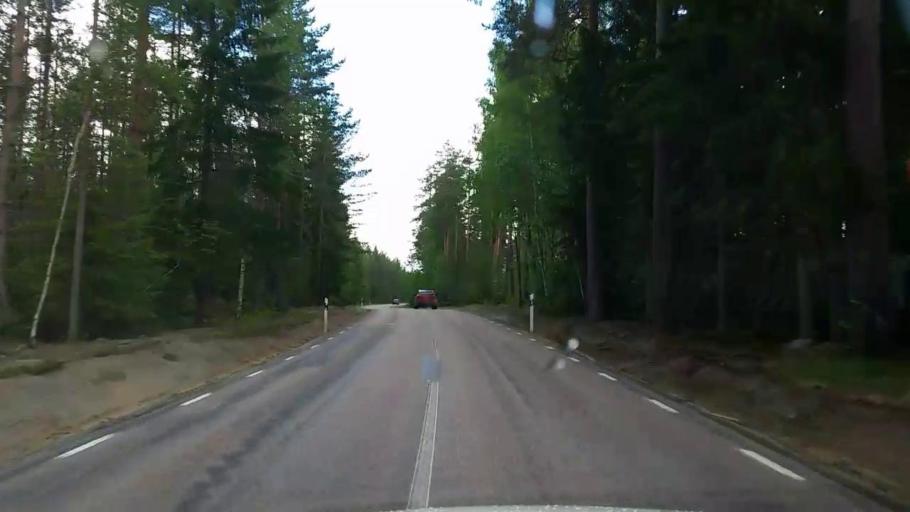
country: SE
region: Vaestmanland
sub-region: Fagersta Kommun
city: Fagersta
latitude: 59.8613
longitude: 15.8425
